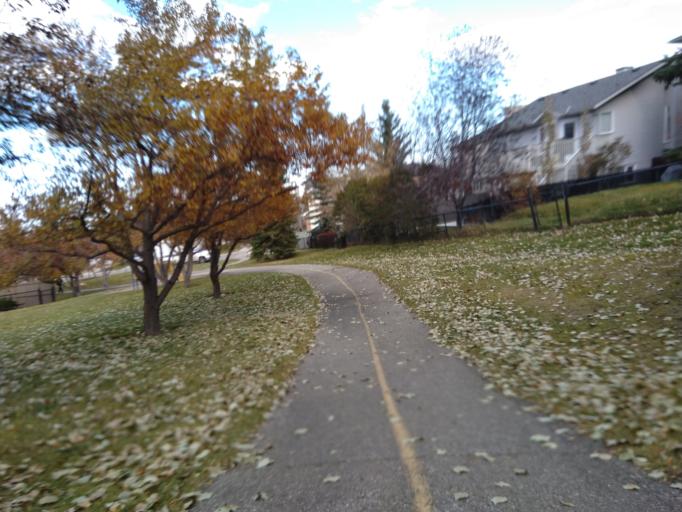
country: CA
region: Alberta
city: Calgary
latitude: 51.1394
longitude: -114.1188
